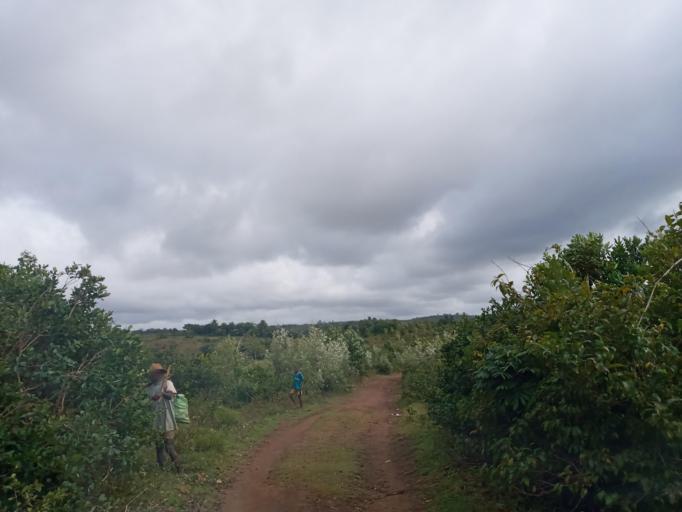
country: MG
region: Atsimo-Atsinanana
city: Vohipaho
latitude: -23.7789
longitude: 47.5389
